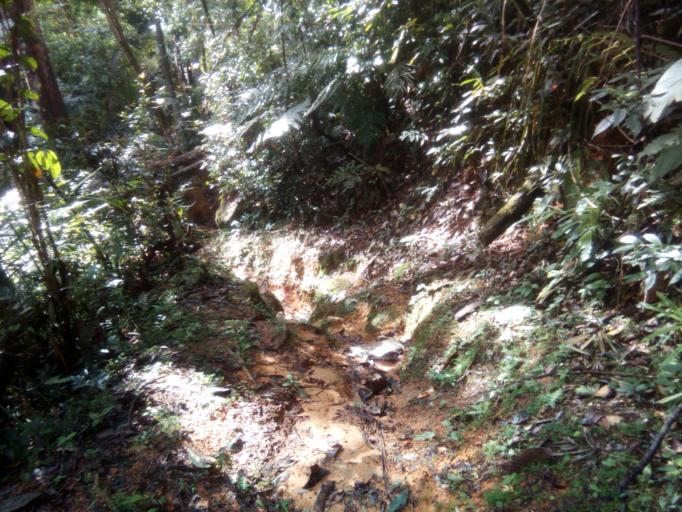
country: MY
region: Penang
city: Tanjung Tokong
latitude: 5.4152
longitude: 100.2580
